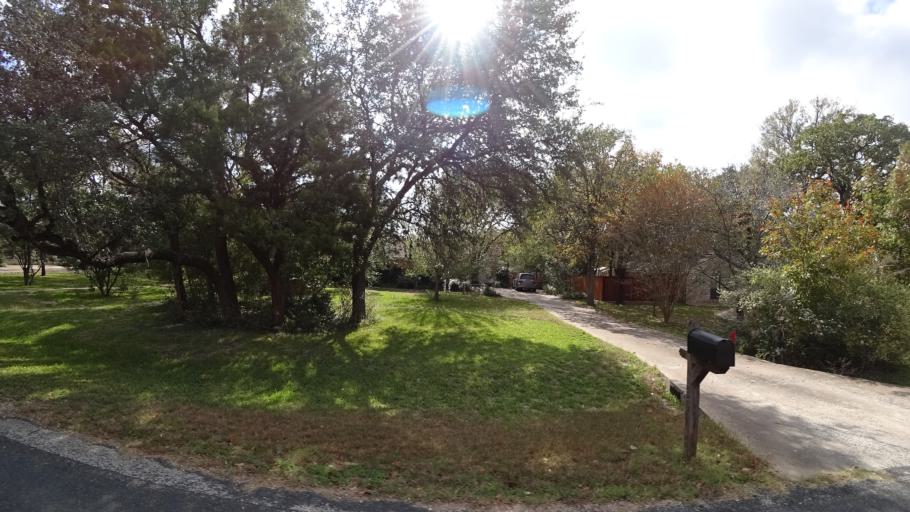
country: US
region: Texas
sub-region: Travis County
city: Shady Hollow
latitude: 30.1616
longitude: -97.8568
